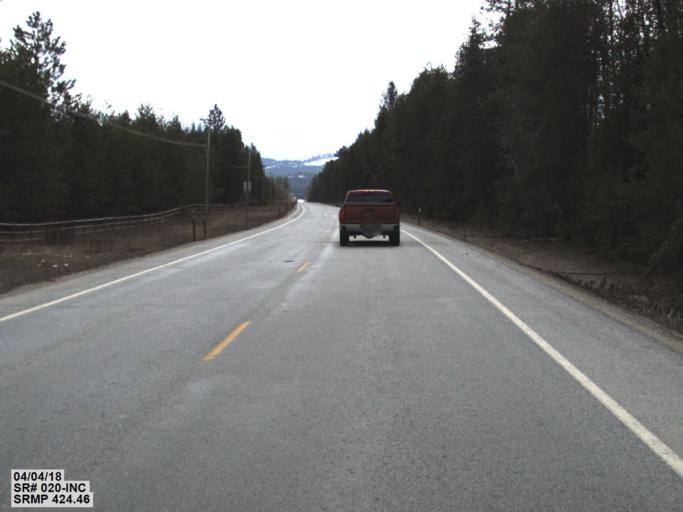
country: US
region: Washington
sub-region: Pend Oreille County
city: Newport
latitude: 48.2658
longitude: -117.2574
